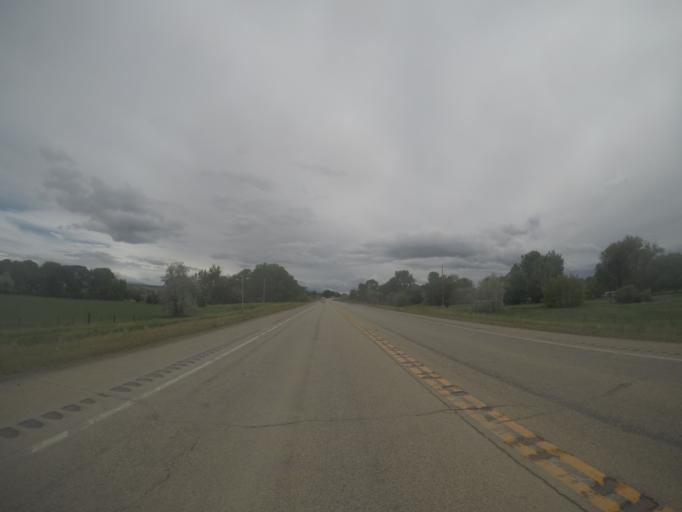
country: US
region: Montana
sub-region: Carbon County
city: Red Lodge
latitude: 45.2657
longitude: -108.9124
